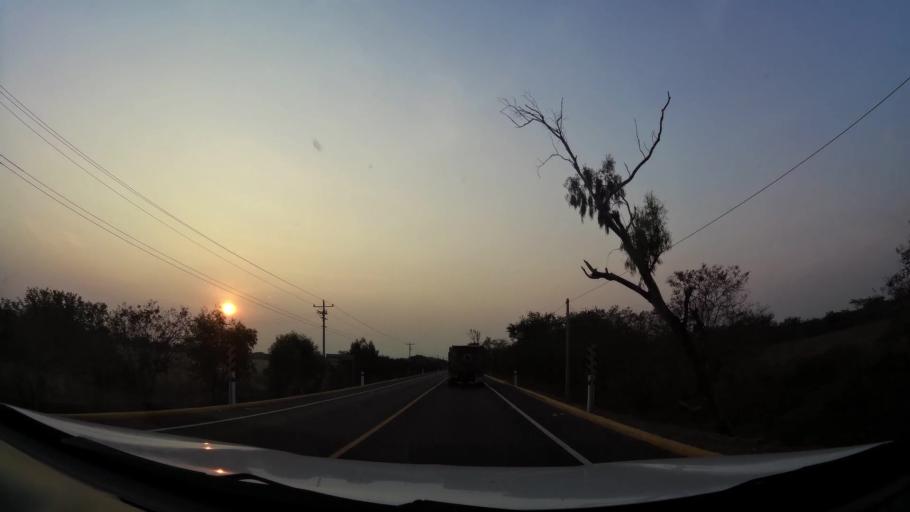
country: NI
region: Leon
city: La Paz Centro
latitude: 12.3130
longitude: -86.7863
